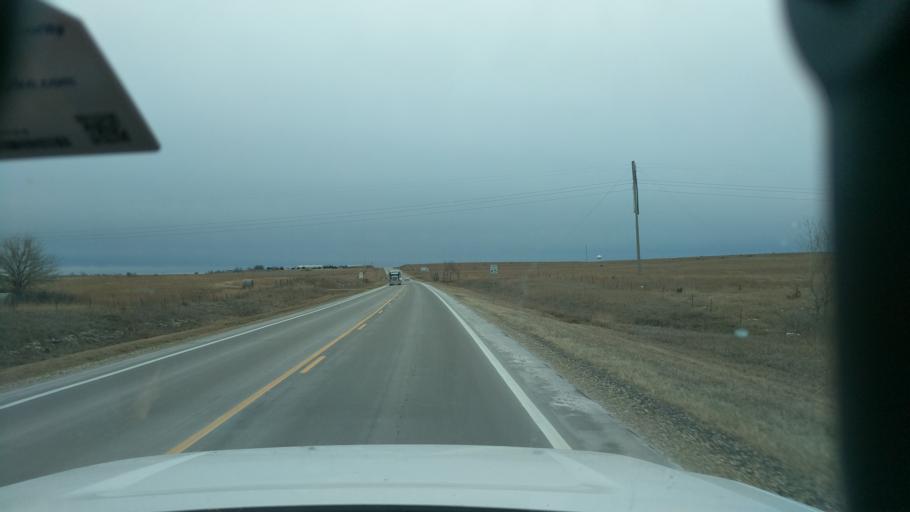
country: US
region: Kansas
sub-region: Dickinson County
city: Herington
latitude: 38.6943
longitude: -96.9301
